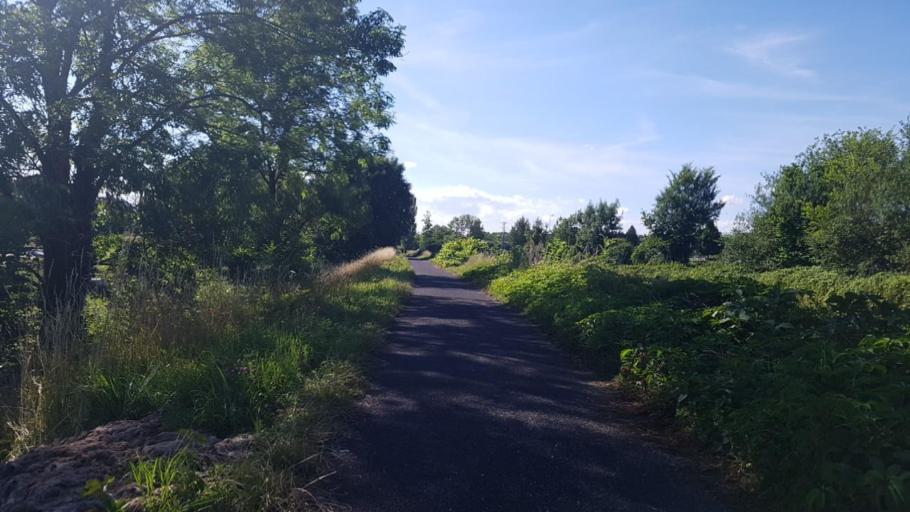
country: FR
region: Lorraine
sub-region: Departement de la Meuse
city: Bar-le-Duc
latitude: 48.7854
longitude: 5.1515
